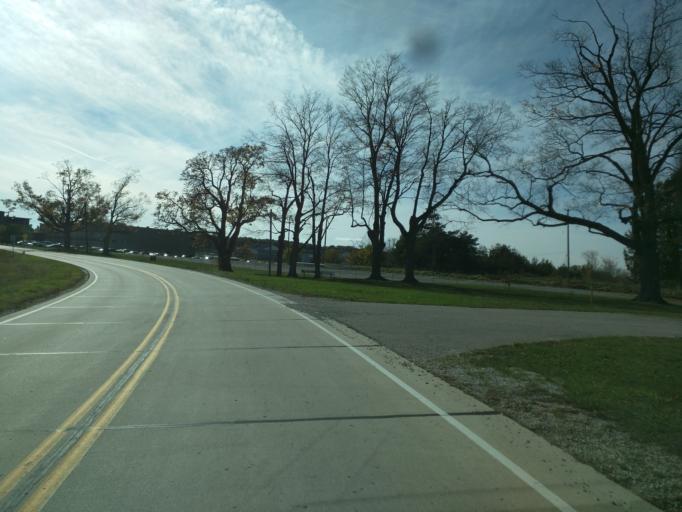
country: US
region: Michigan
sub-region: Ingham County
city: Edgemont Park
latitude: 42.7716
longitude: -84.5670
